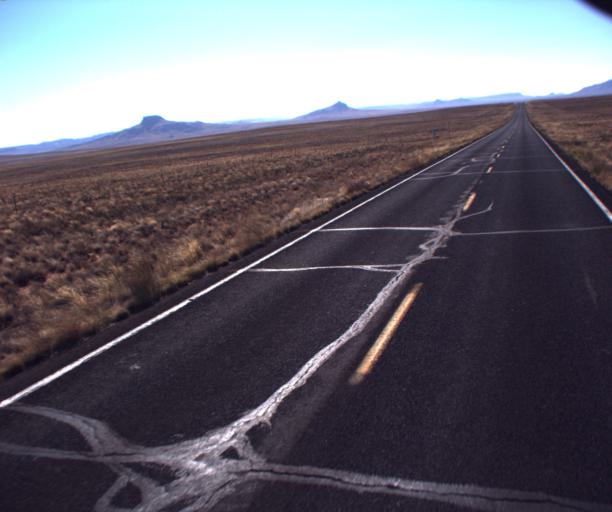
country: US
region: Arizona
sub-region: Navajo County
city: First Mesa
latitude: 35.6275
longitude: -110.4809
